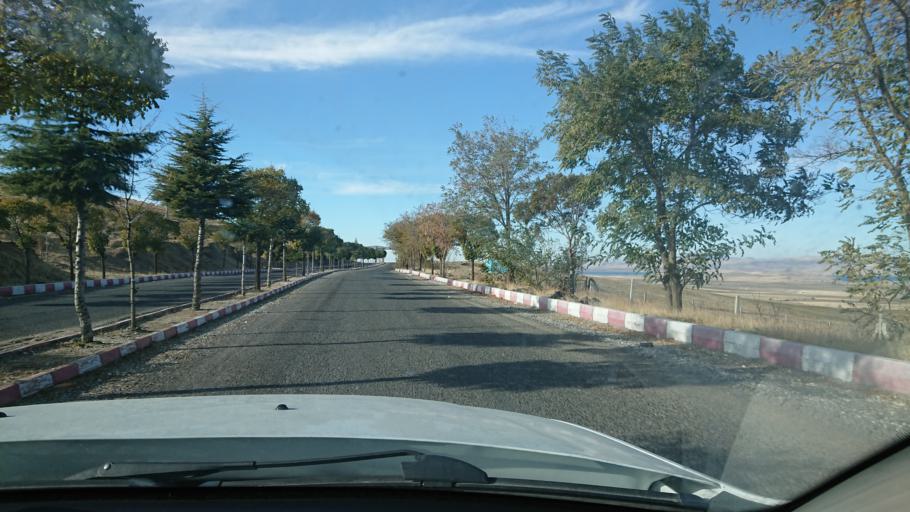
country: TR
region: Aksaray
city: Sariyahsi
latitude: 38.9662
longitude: 33.8741
